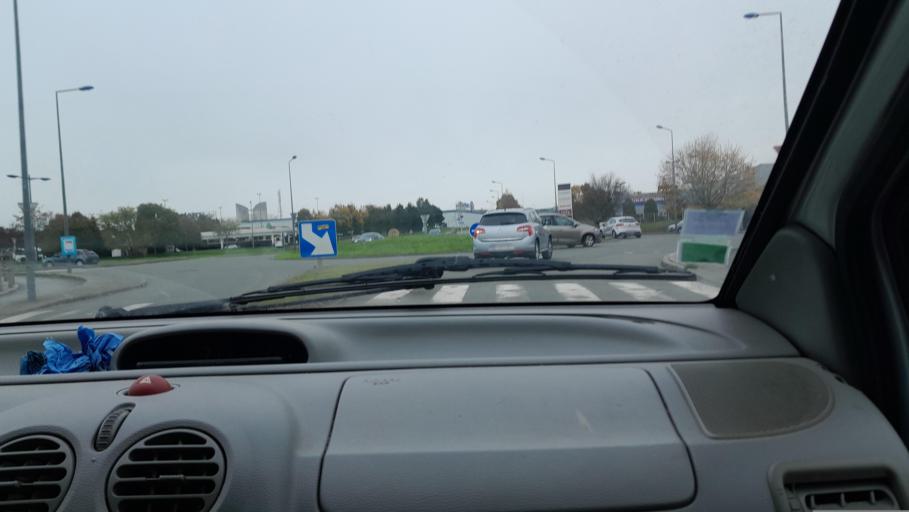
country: FR
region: Pays de la Loire
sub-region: Departement de la Mayenne
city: Saint-Berthevin
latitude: 48.0664
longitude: -0.8124
